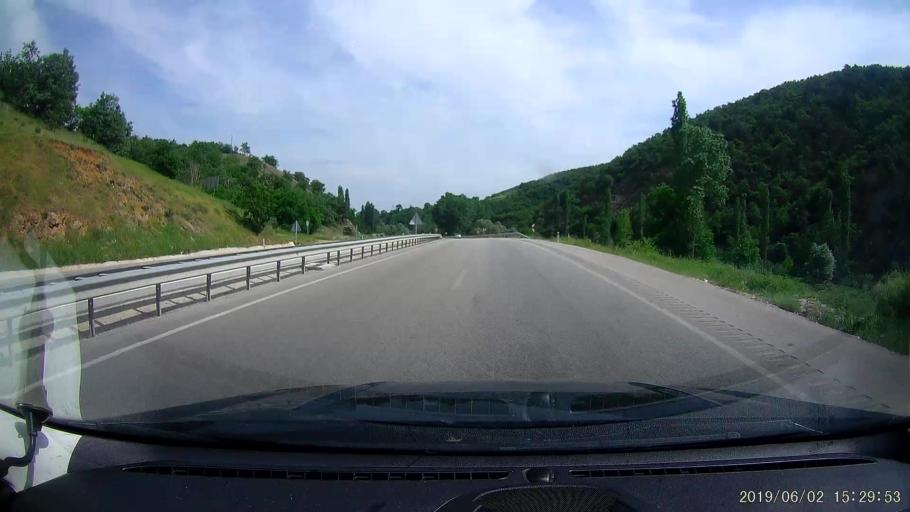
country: TR
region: Amasya
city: Saraycik
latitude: 40.9626
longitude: 35.0978
